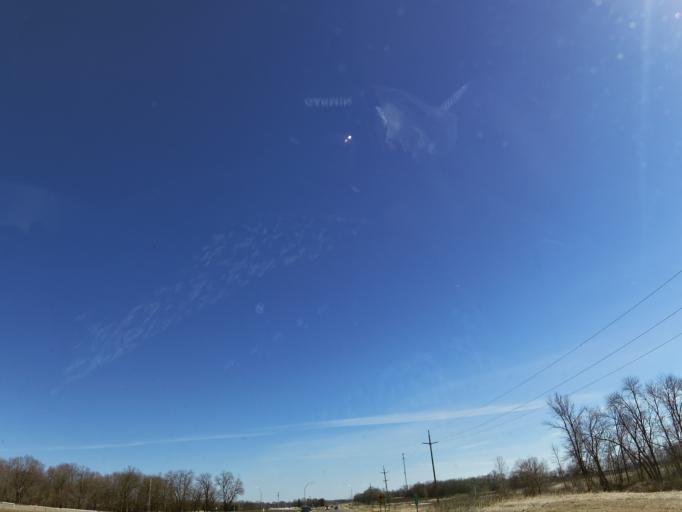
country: US
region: Minnesota
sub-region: Wright County
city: Buffalo
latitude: 45.2021
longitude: -93.9111
